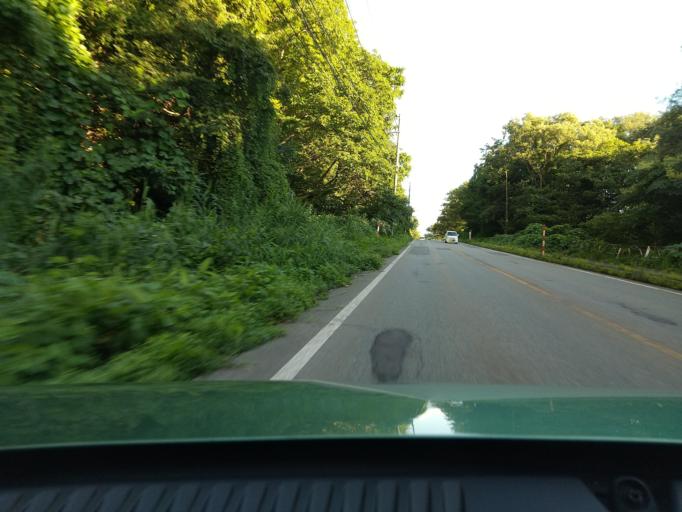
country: JP
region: Akita
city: Kakunodatemachi
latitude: 39.7353
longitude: 140.7182
